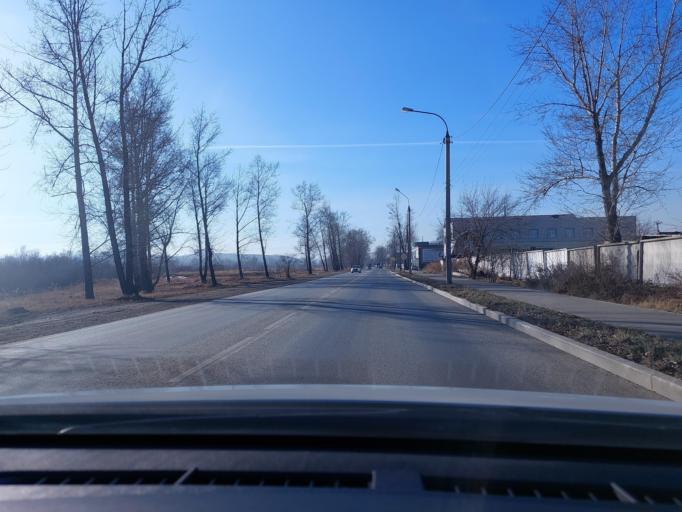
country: RU
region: Irkutsk
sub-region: Irkutskiy Rayon
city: Irkutsk
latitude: 52.3084
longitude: 104.2590
